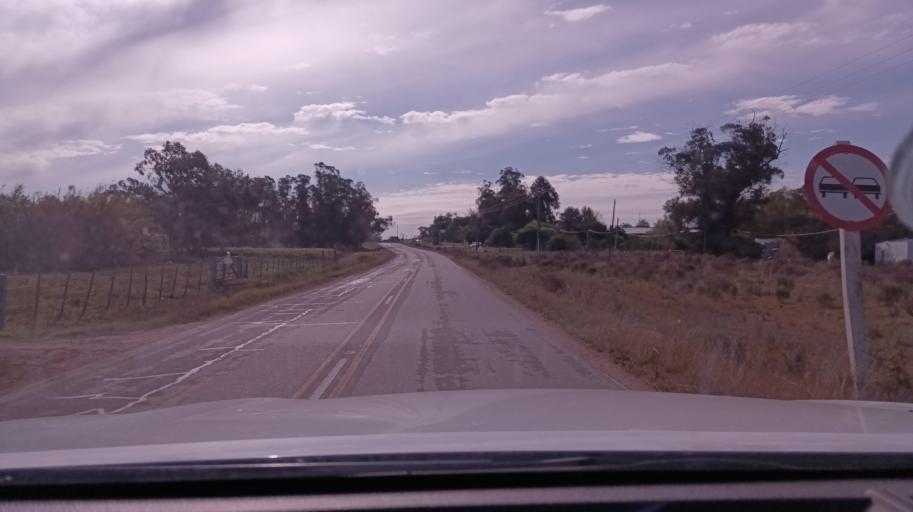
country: UY
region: Canelones
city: Sauce
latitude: -34.6306
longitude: -56.1101
